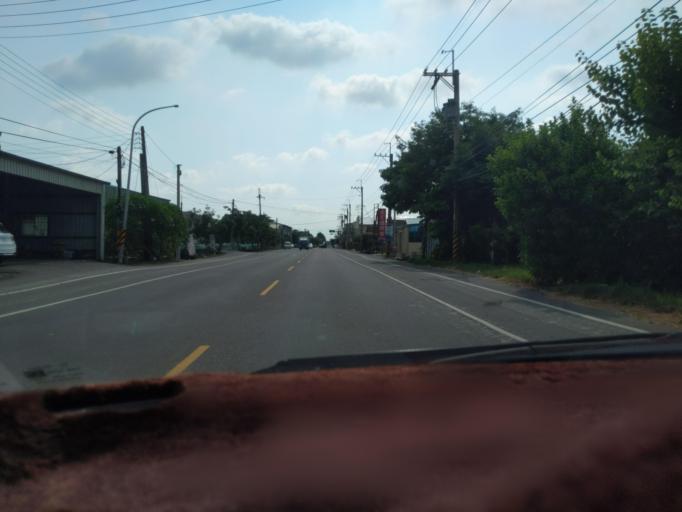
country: TW
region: Taiwan
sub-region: Yunlin
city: Douliu
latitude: 23.7968
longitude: 120.4306
